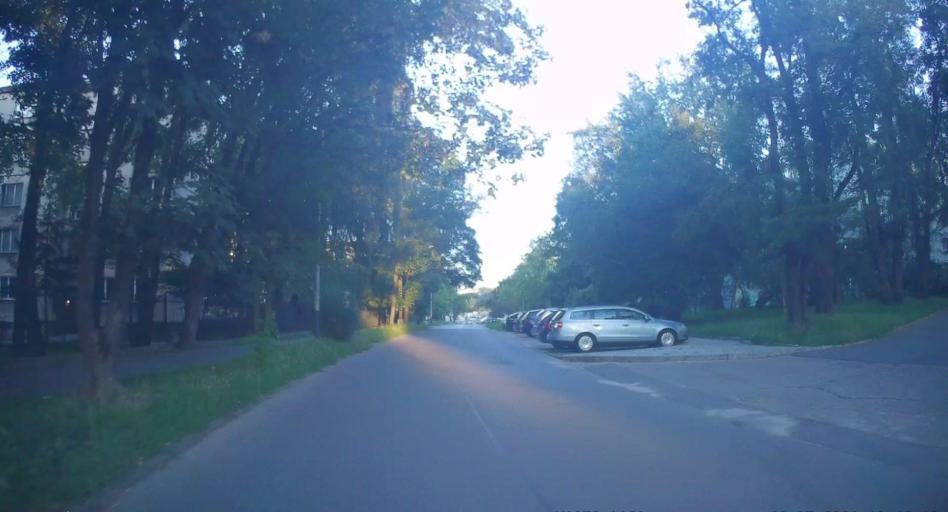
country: PL
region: Lesser Poland Voivodeship
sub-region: Powiat wielicki
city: Czarnochowice
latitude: 50.0131
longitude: 20.0068
